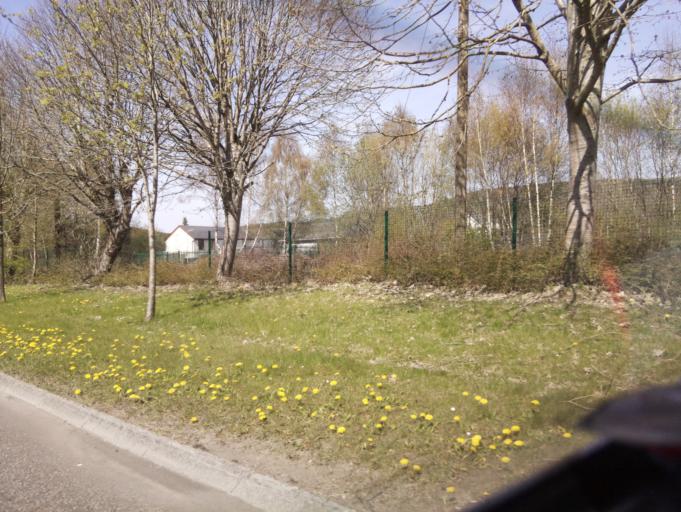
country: GB
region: Wales
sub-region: Rhondda Cynon Taf
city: Aberdare
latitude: 51.7186
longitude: -3.4482
